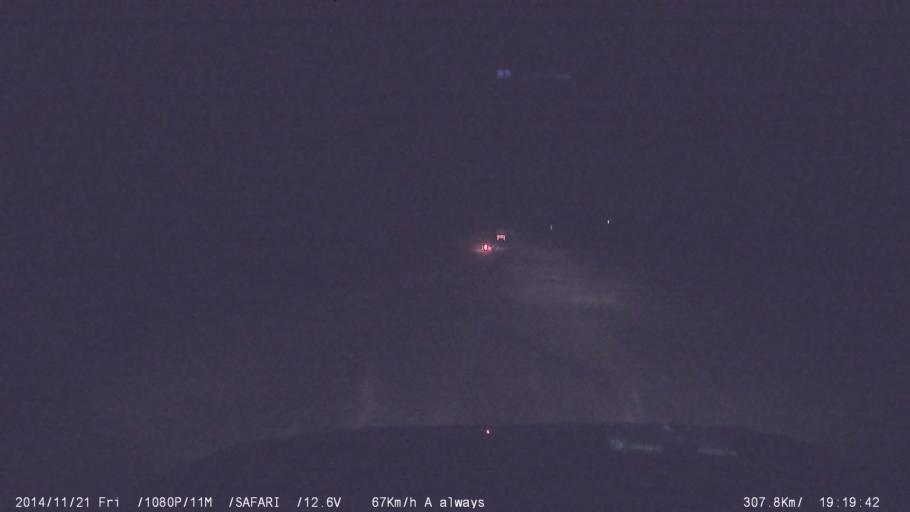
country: IN
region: Tamil Nadu
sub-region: Kancheepuram
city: Singapperumalkovil
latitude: 12.8079
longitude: 79.9732
